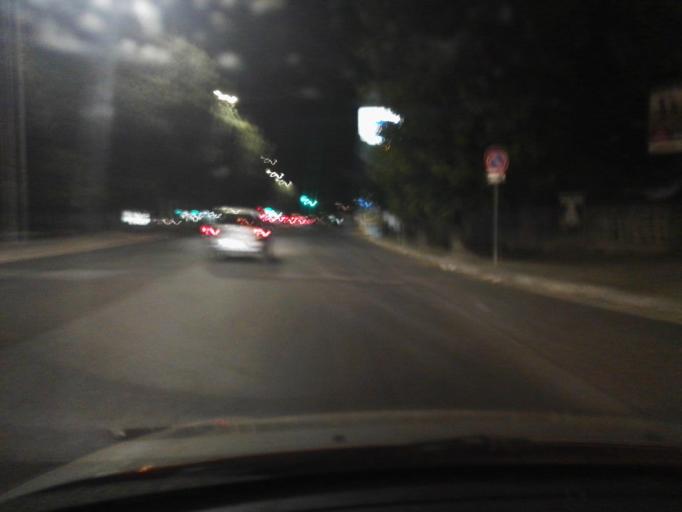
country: VA
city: Vatican City
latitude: 41.8585
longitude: 12.4708
